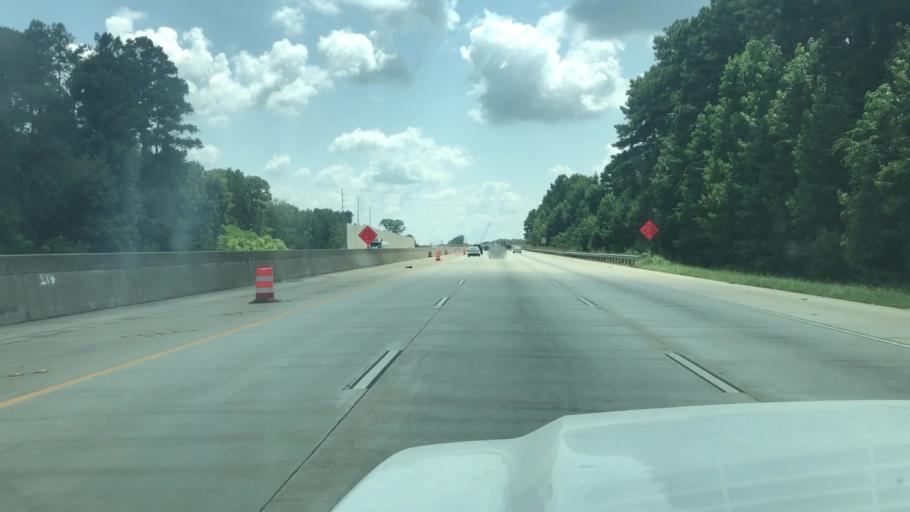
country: US
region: Georgia
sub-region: Coweta County
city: East Newnan
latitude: 33.3696
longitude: -84.7591
